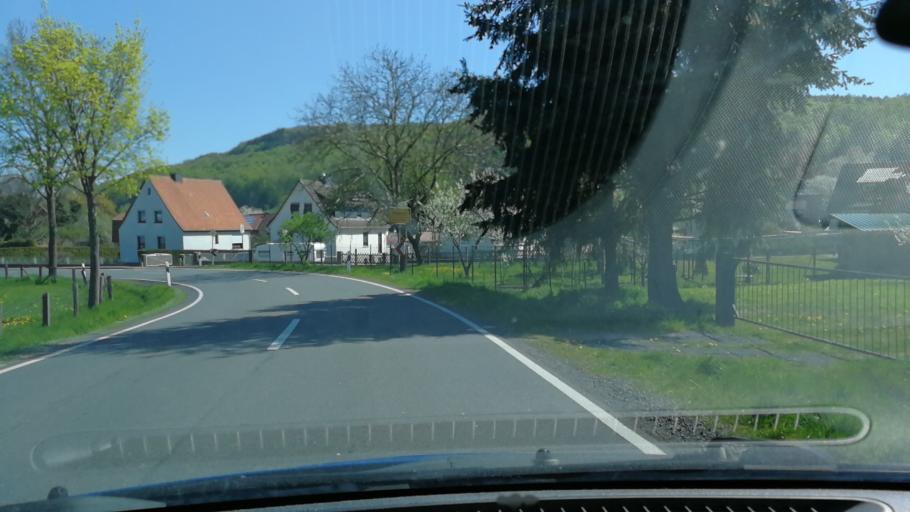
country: DE
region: Lower Saxony
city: Hardegsen
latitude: 51.6308
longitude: 9.8040
